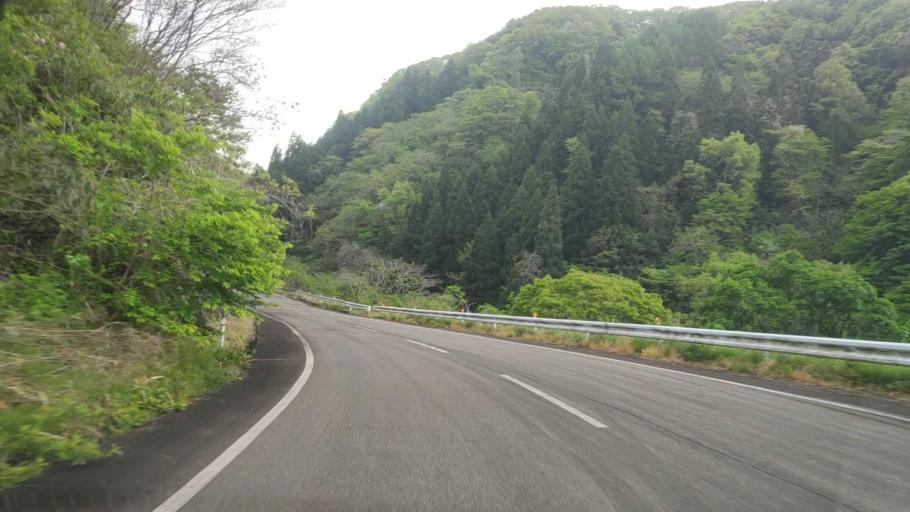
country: JP
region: Niigata
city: Kamo
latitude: 37.7121
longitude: 139.0928
